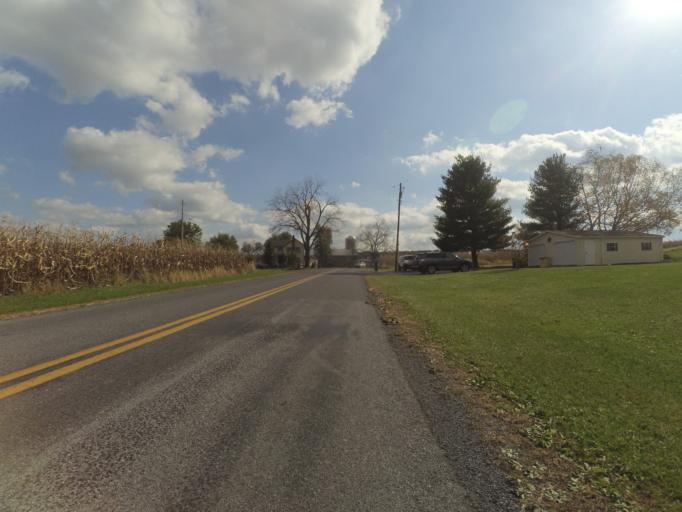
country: US
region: Pennsylvania
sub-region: Centre County
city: Houserville
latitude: 40.8740
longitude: -77.8296
